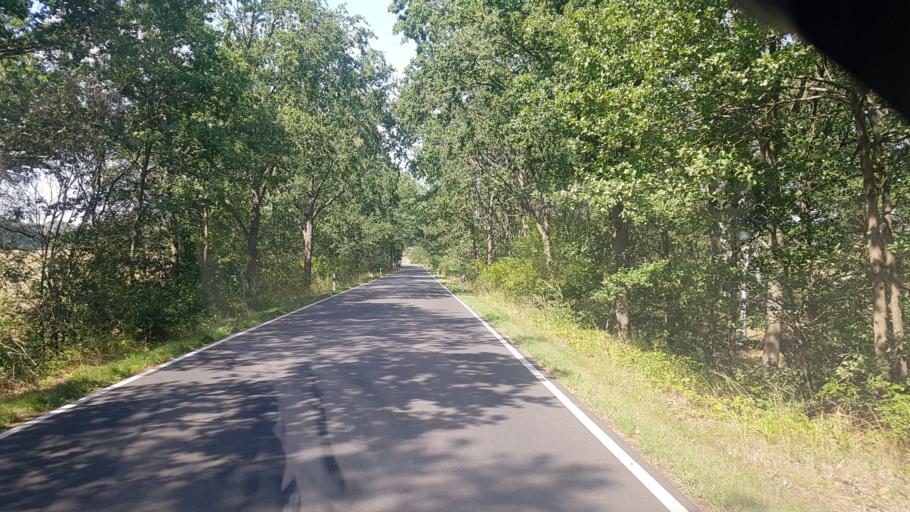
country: DE
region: Brandenburg
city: Cottbus
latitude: 51.7072
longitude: 14.4260
